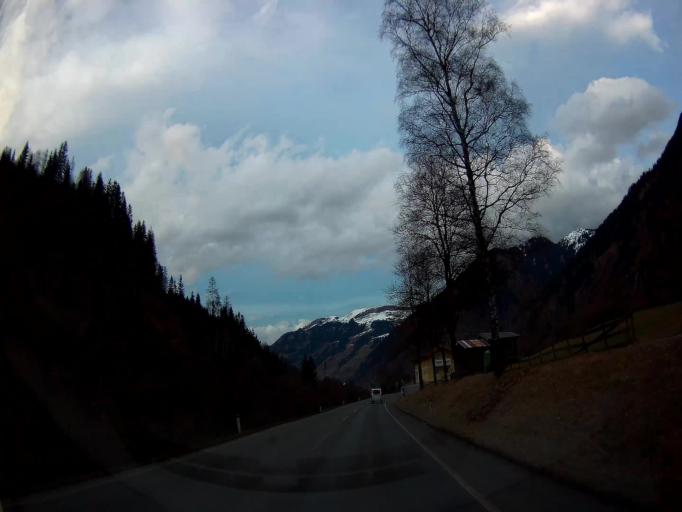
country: AT
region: Salzburg
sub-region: Politischer Bezirk Sankt Johann im Pongau
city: Bad Hofgastein
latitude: 47.2032
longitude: 13.1062
